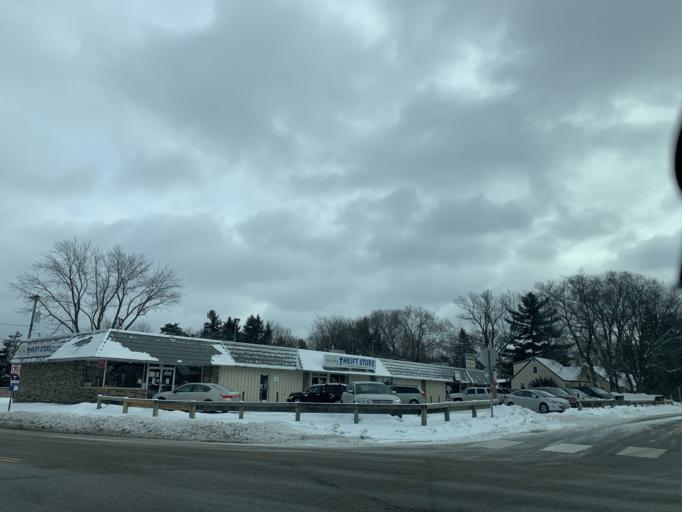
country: US
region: Minnesota
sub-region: Ramsey County
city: Little Canada
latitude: 45.0239
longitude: -93.0941
